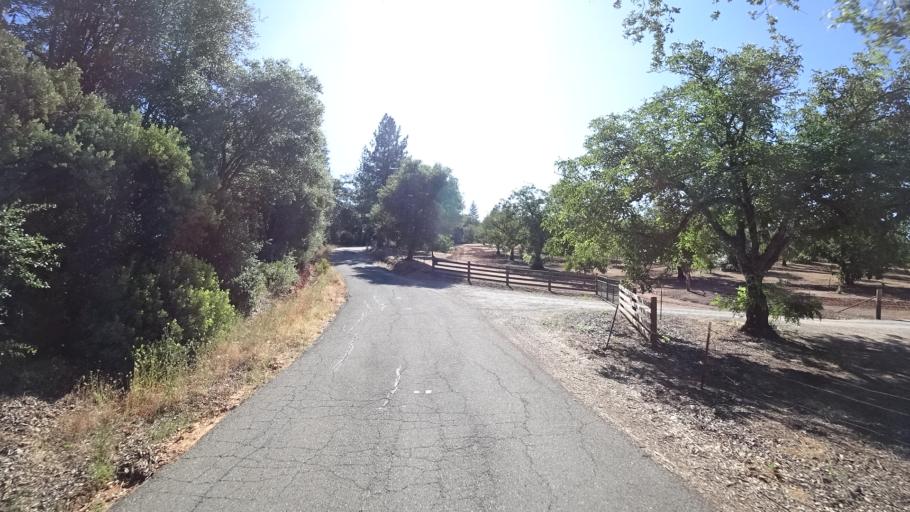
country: US
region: California
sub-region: Amador County
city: Pioneer
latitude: 38.3993
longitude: -120.5475
